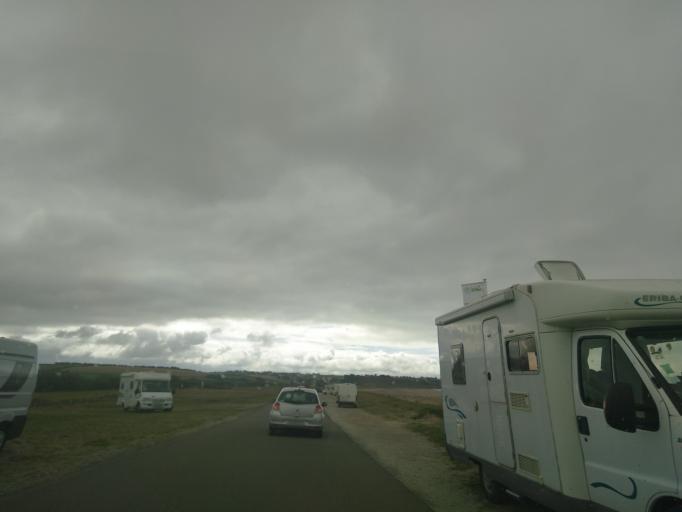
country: FR
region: Brittany
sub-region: Departement du Finistere
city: Plomodiern
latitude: 48.1868
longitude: -4.2976
